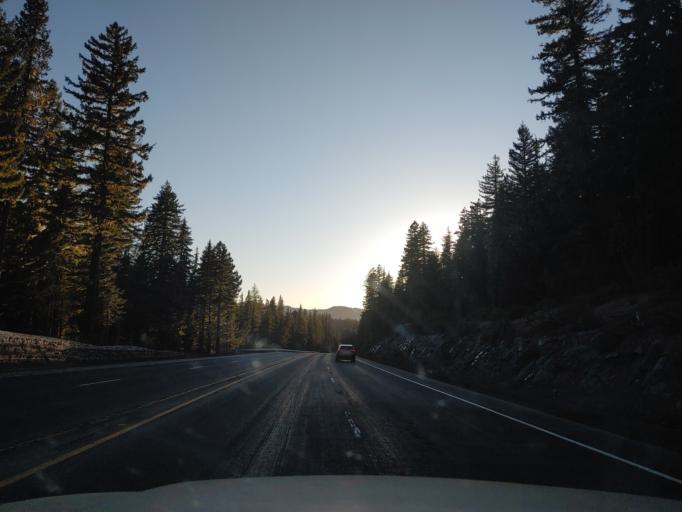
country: US
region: Oregon
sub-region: Lane County
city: Oakridge
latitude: 43.6171
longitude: -122.0865
